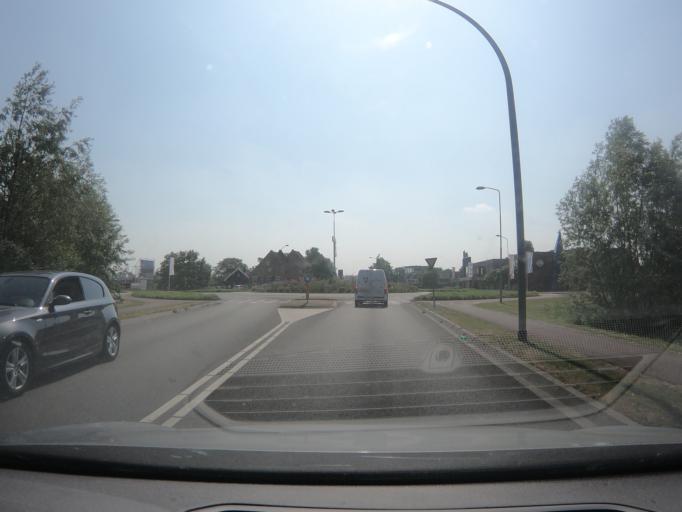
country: NL
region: Gelderland
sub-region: Gemeente Westervoort
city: Westervoort
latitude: 51.9618
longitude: 5.9796
